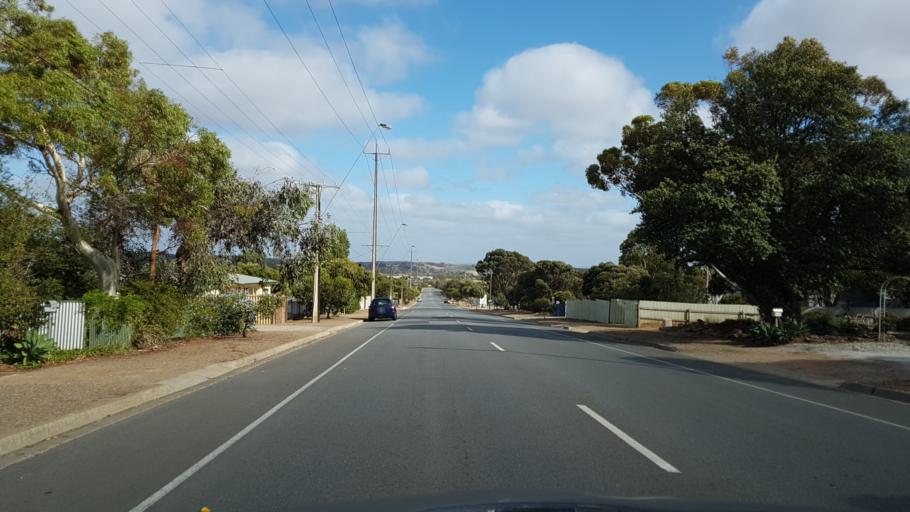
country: AU
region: South Australia
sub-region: Murray Bridge
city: Murray Bridge
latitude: -35.1206
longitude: 139.2516
